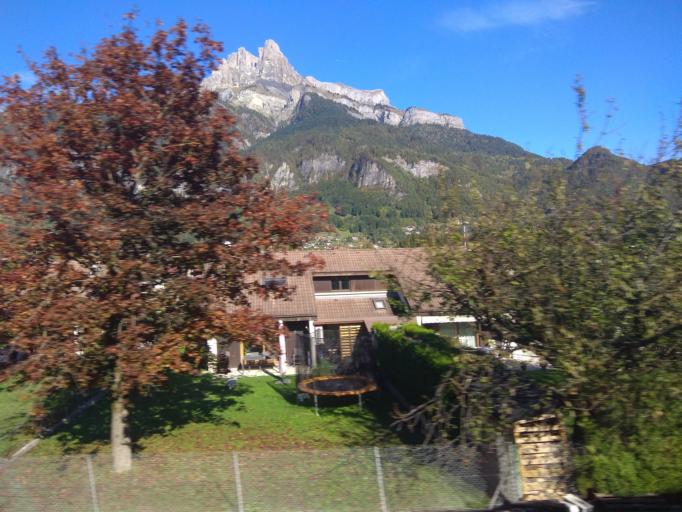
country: FR
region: Rhone-Alpes
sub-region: Departement de la Haute-Savoie
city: Sallanches
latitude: 45.9305
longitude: 6.6383
